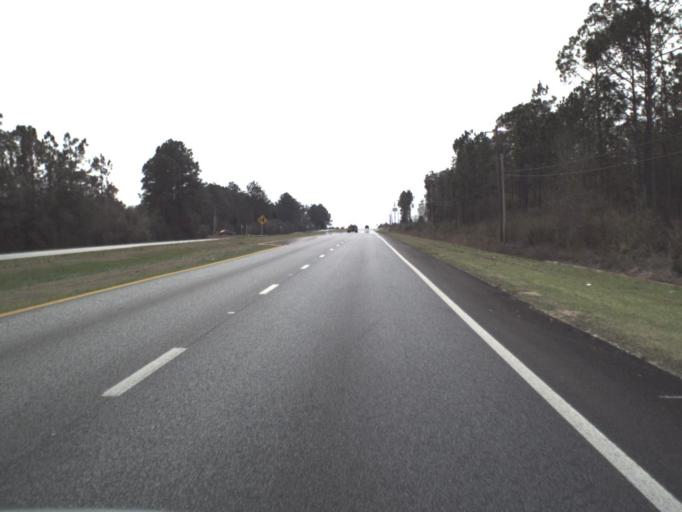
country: US
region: Florida
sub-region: Bay County
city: Youngstown
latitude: 30.3187
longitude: -85.4586
